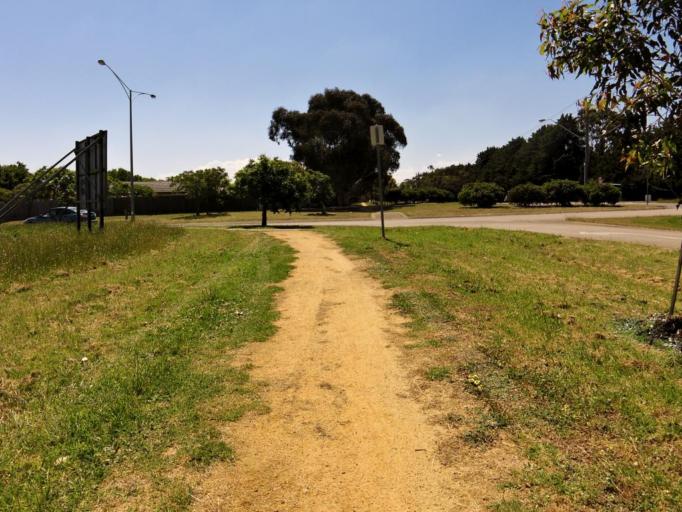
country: AU
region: Victoria
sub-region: Casey
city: Narre Warren South
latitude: -38.0462
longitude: 145.2948
